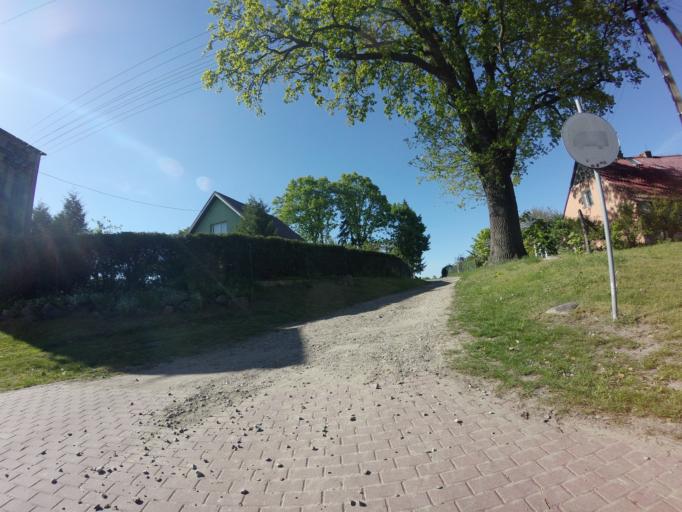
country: PL
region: West Pomeranian Voivodeship
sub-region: Powiat stargardzki
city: Dolice
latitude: 53.1608
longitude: 15.2850
